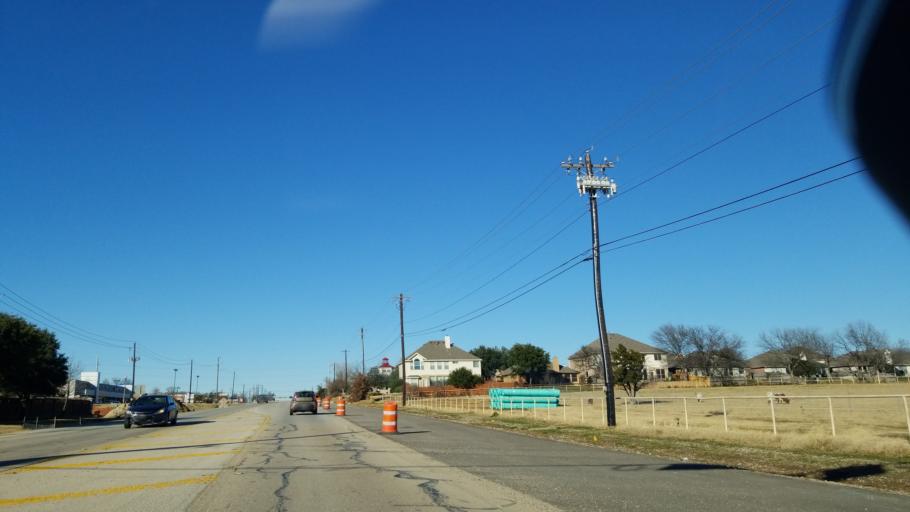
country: US
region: Texas
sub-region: Denton County
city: Corinth
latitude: 33.1421
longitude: -97.1052
